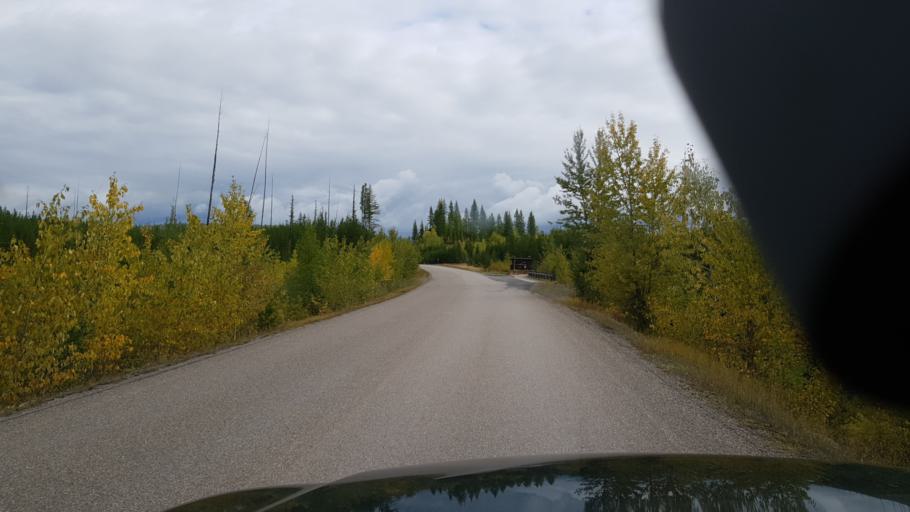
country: US
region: Montana
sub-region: Flathead County
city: Columbia Falls
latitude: 48.6220
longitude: -114.1346
